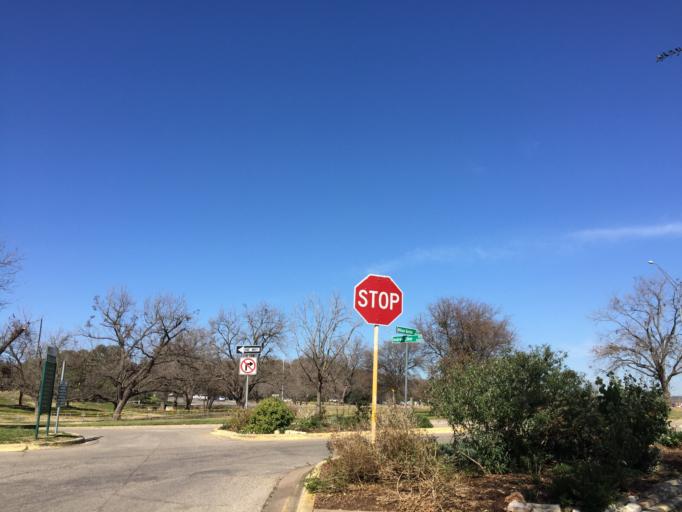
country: US
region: Texas
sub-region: Travis County
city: Rollingwood
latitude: 30.2657
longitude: -97.7692
